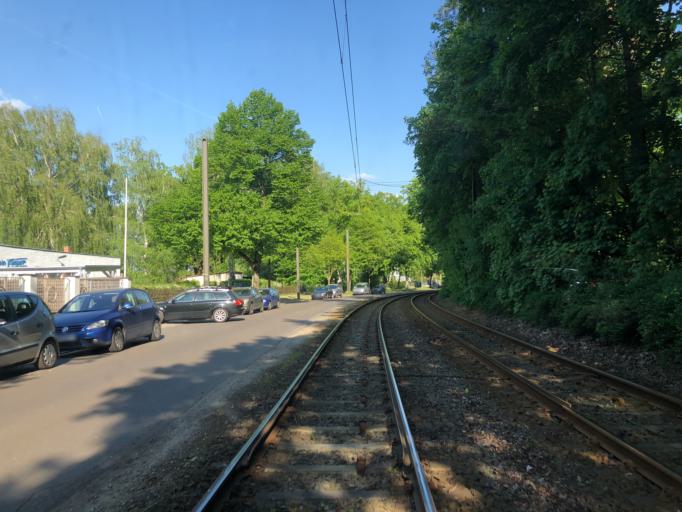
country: DE
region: Berlin
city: Grunau
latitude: 52.4109
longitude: 13.5952
